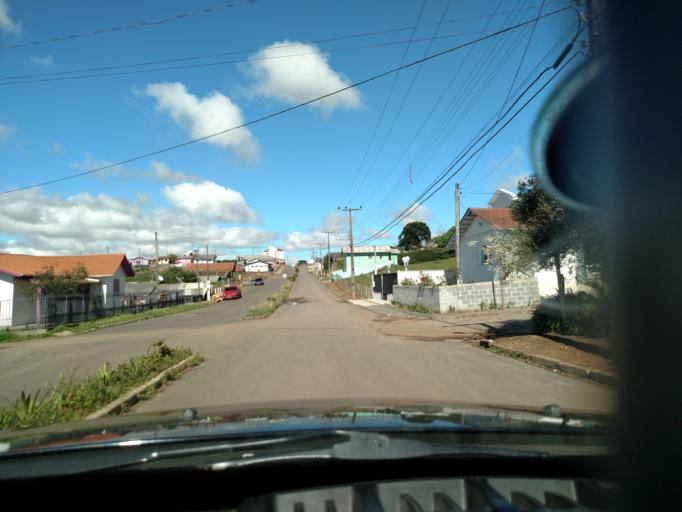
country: BR
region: Santa Catarina
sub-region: Sao Joaquim
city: Sao Joaquim
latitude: -28.2907
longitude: -49.9248
